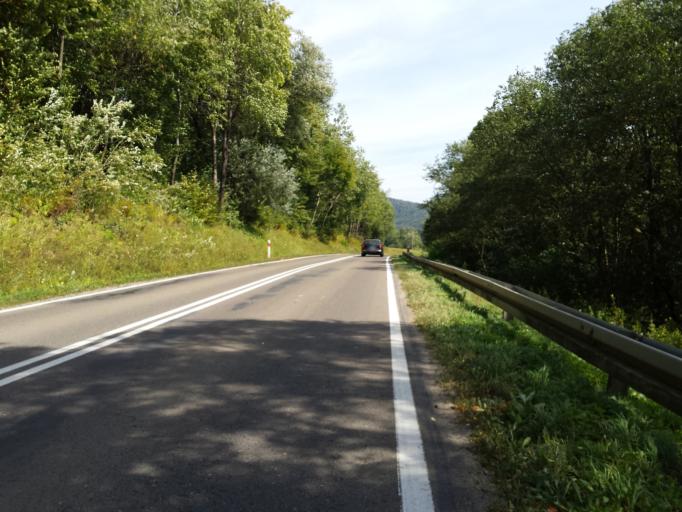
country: PL
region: Subcarpathian Voivodeship
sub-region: Powiat leski
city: Lesko
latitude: 49.4315
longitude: 22.3347
